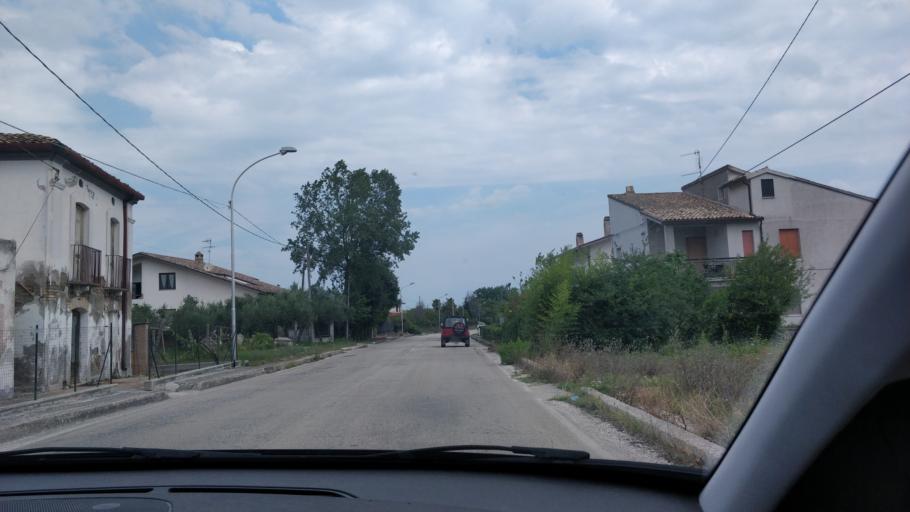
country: IT
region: Abruzzo
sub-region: Provincia di Chieti
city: San Vito Chietino
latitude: 42.2821
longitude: 14.4386
